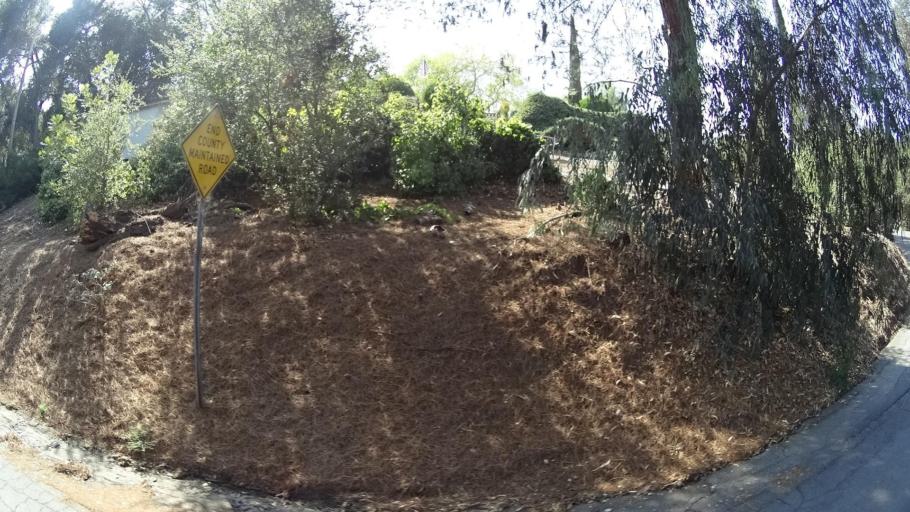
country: US
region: California
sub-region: San Diego County
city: Escondido
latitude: 33.1030
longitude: -117.0518
